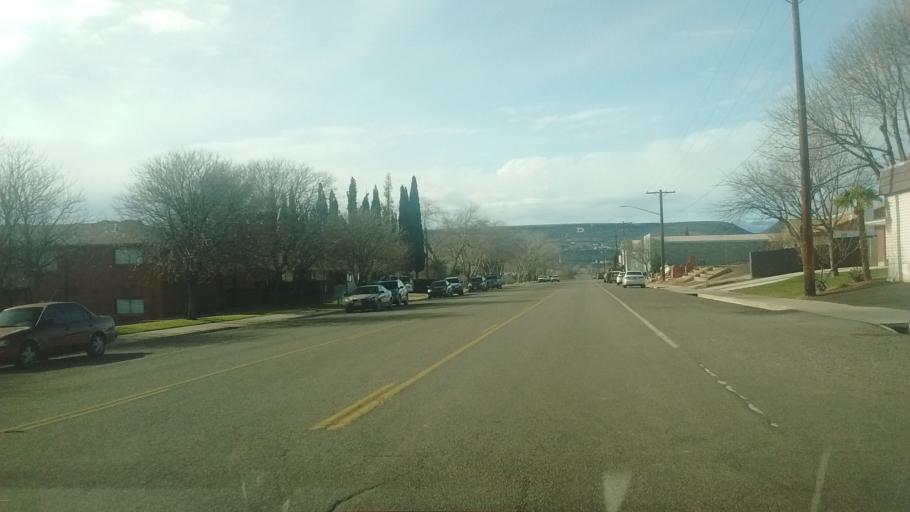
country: US
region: Utah
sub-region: Washington County
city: Saint George
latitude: 37.1082
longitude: -113.5664
